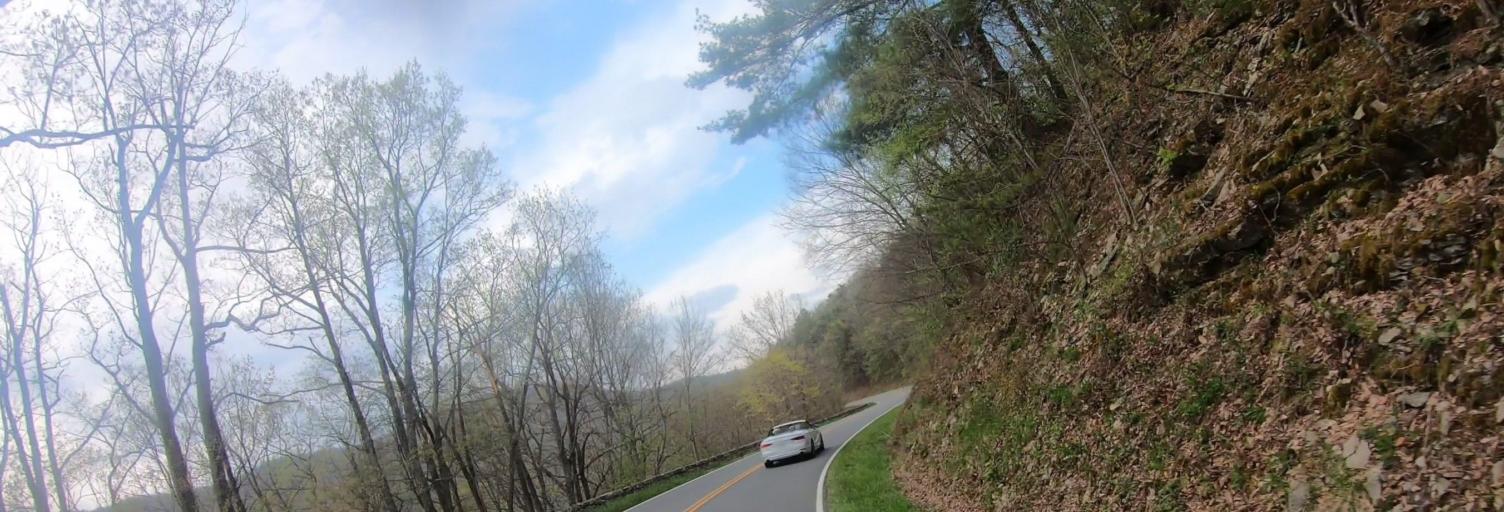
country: US
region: Virginia
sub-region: Rockingham County
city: Grottoes
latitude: 38.2013
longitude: -78.7545
